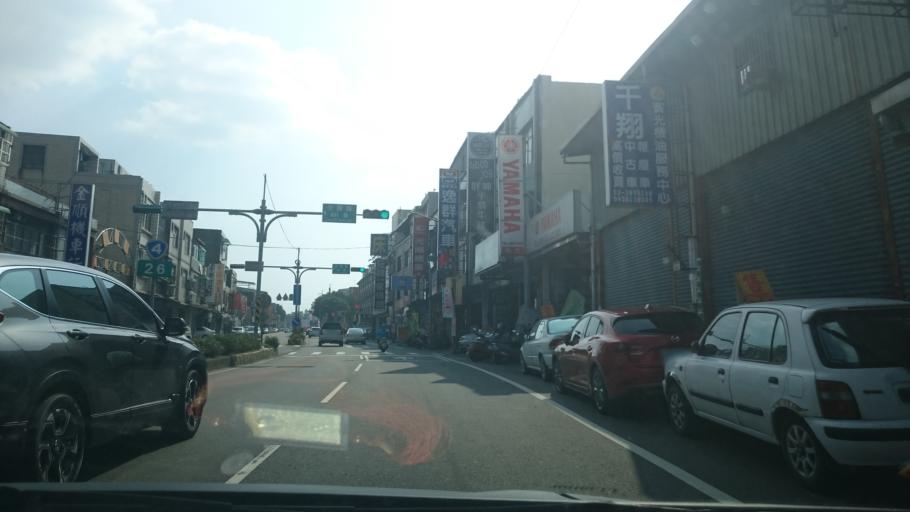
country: TW
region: Taiwan
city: Daxi
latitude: 24.9068
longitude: 121.2857
